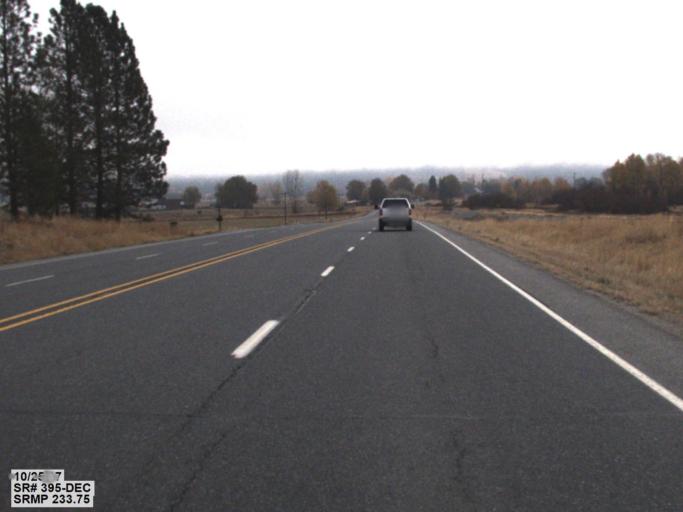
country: US
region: Washington
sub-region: Stevens County
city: Colville
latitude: 48.5849
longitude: -117.9705
